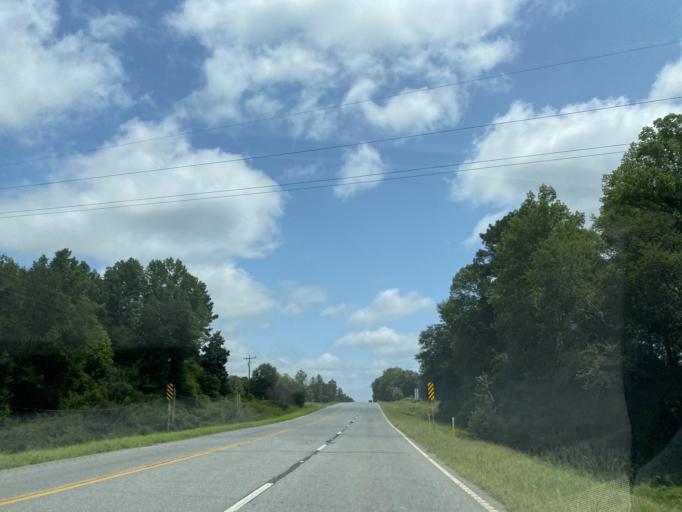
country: US
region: Georgia
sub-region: Telfair County
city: McRae
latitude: 32.0848
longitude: -82.8787
